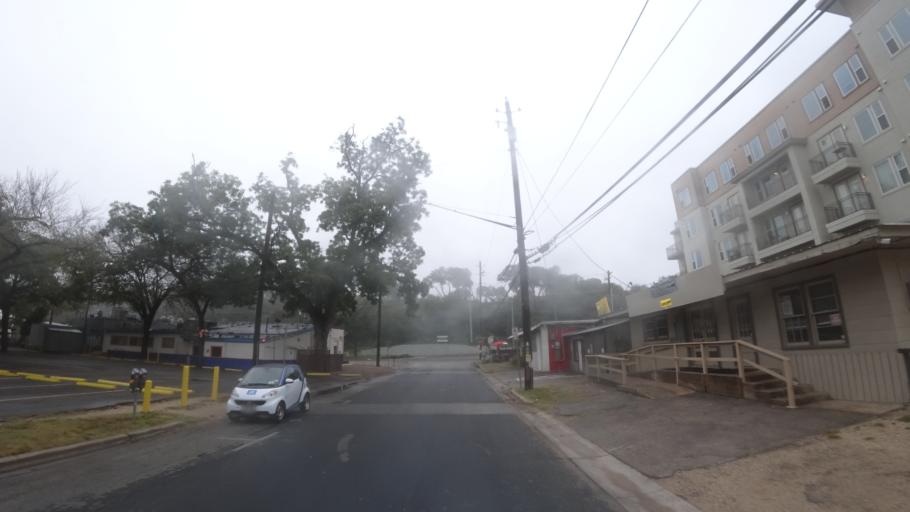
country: US
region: Texas
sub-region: Travis County
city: Austin
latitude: 30.2643
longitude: -97.7633
